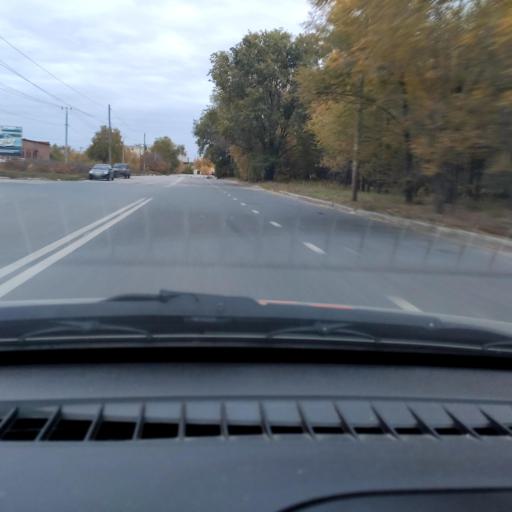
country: RU
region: Samara
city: Tol'yatti
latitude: 53.5623
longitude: 49.2955
